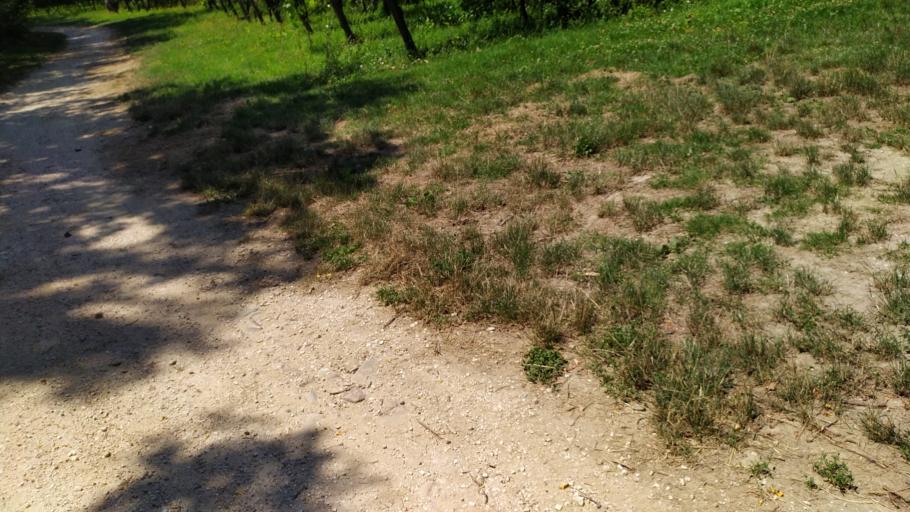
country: IT
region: Emilia-Romagna
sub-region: Forli-Cesena
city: Castrocaro Terme e Terra del Sole
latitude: 44.1971
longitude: 11.9792
